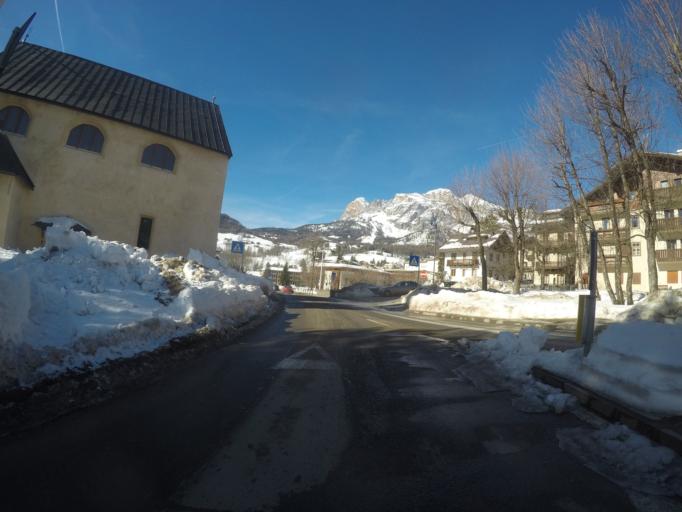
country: IT
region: Veneto
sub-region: Provincia di Belluno
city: Cortina d'Ampezzo
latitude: 46.5353
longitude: 12.1391
